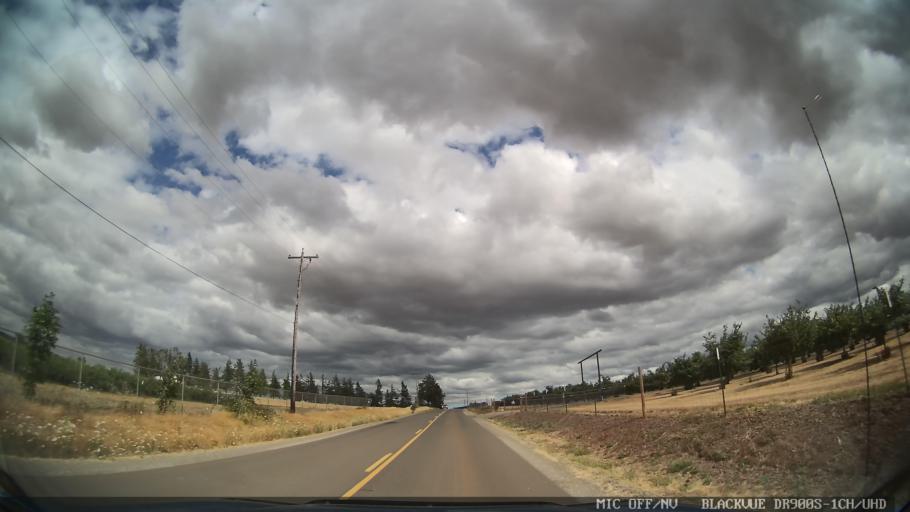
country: US
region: Oregon
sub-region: Marion County
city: Sublimity
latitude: 44.8661
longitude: -122.7686
